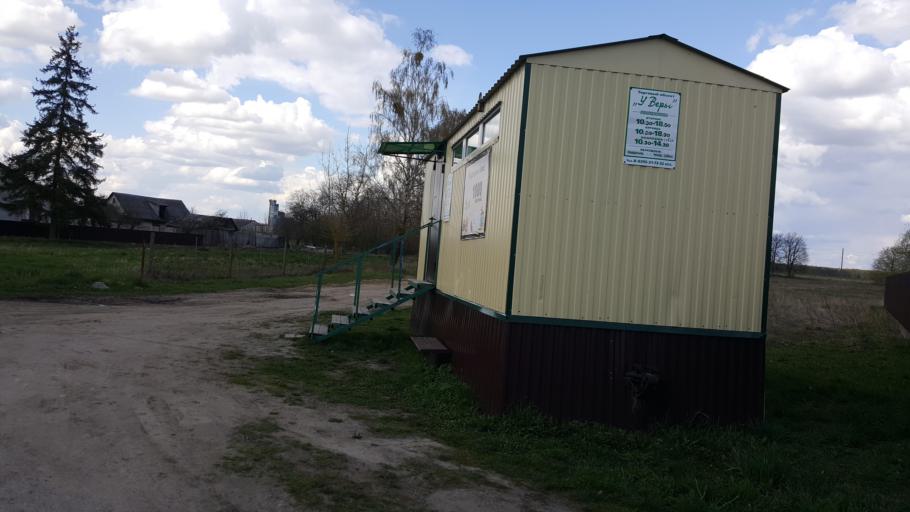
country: BY
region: Brest
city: Kamyanyets
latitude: 52.4099
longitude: 23.6262
